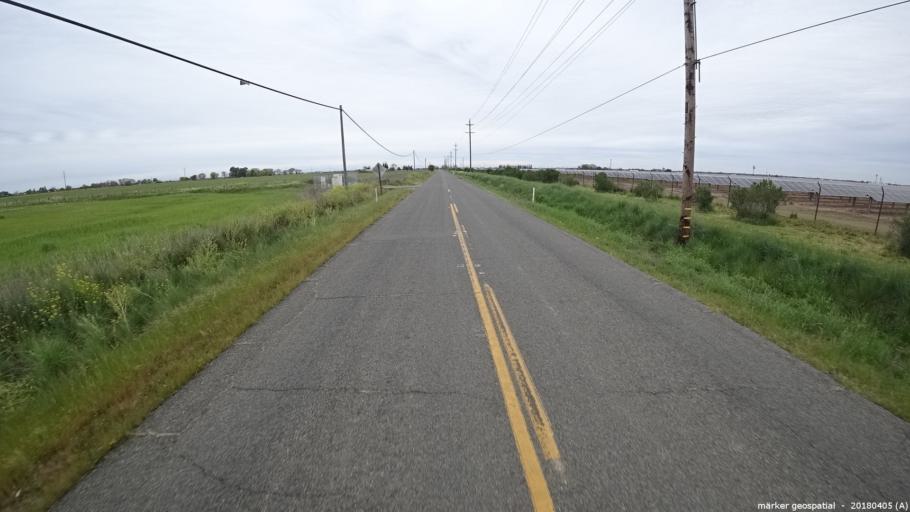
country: US
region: California
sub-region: Sacramento County
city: Laguna
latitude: 38.3507
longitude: -121.4157
